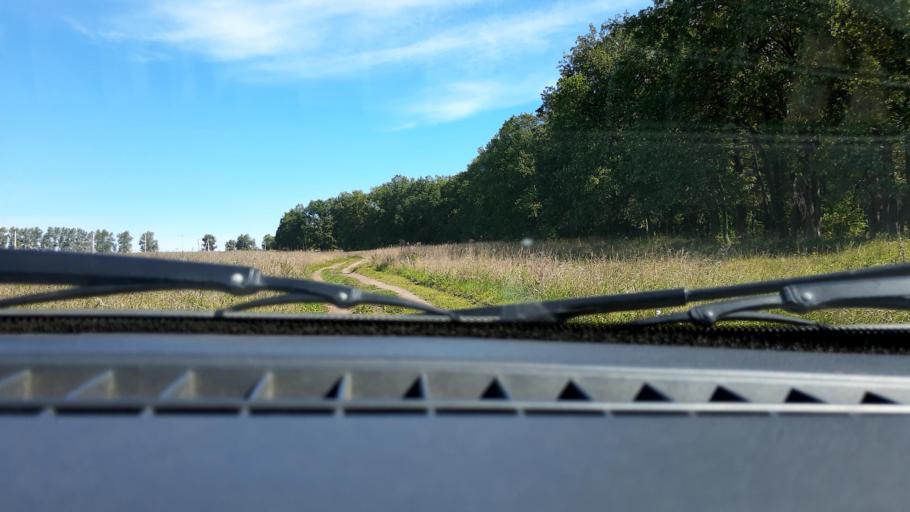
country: RU
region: Bashkortostan
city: Mikhaylovka
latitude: 54.8228
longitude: 55.7928
